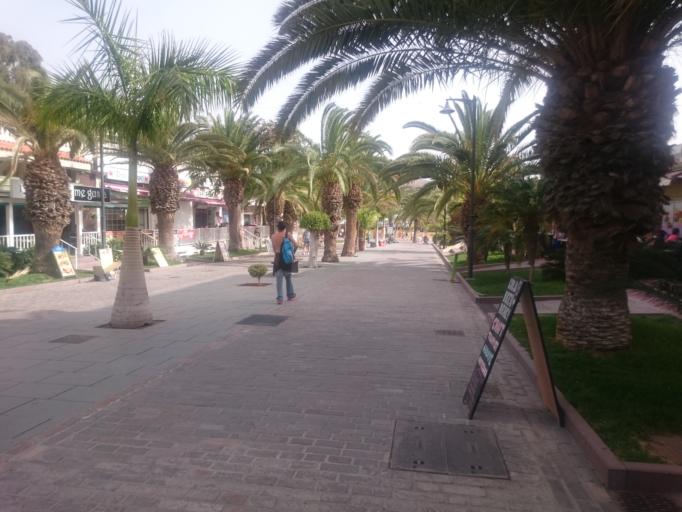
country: ES
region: Canary Islands
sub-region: Provincia de Santa Cruz de Tenerife
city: Playa de las Americas
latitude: 28.0510
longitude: -16.7159
